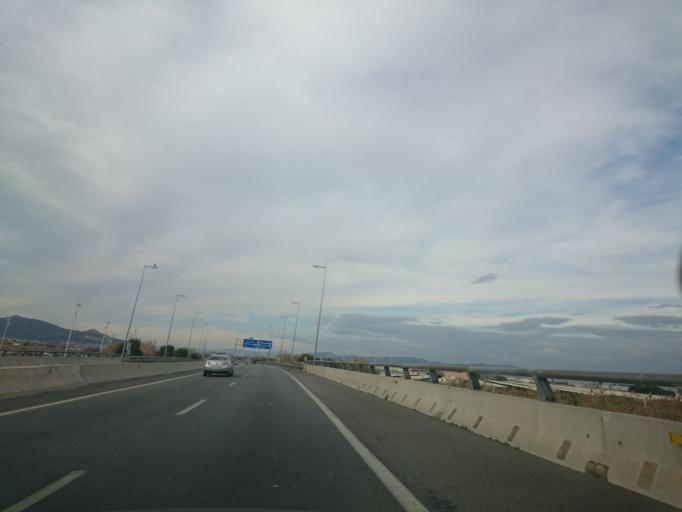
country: ES
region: Catalonia
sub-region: Provincia de Barcelona
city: Viladecans
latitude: 41.2854
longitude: 2.0527
